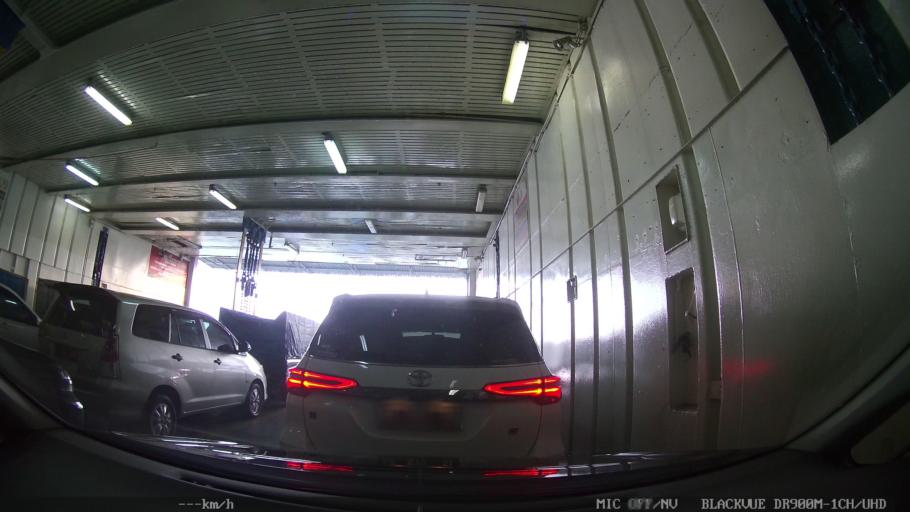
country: ID
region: Lampung
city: Penengahan
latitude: -5.8657
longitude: 105.7578
